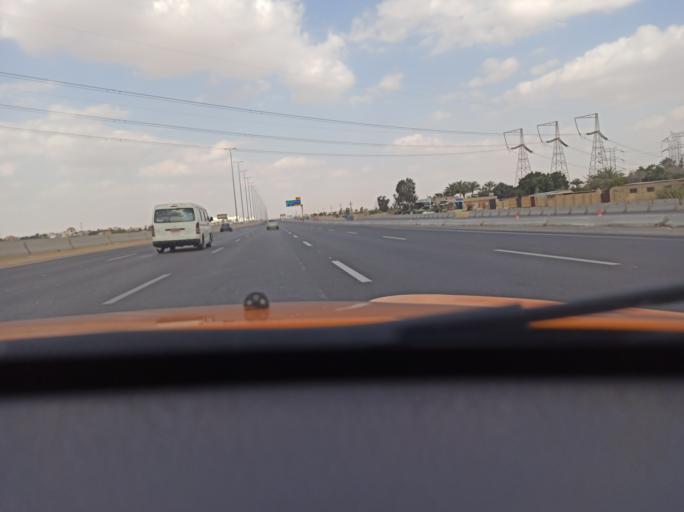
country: EG
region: Eastern Province
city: Bilbays
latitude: 30.1868
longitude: 31.6315
